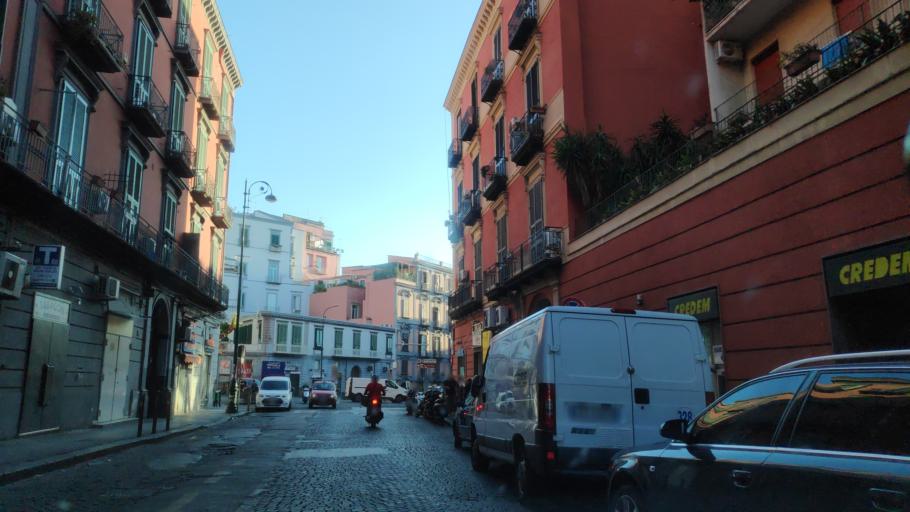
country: IT
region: Campania
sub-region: Provincia di Napoli
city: Napoli
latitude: 40.8509
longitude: 14.2422
